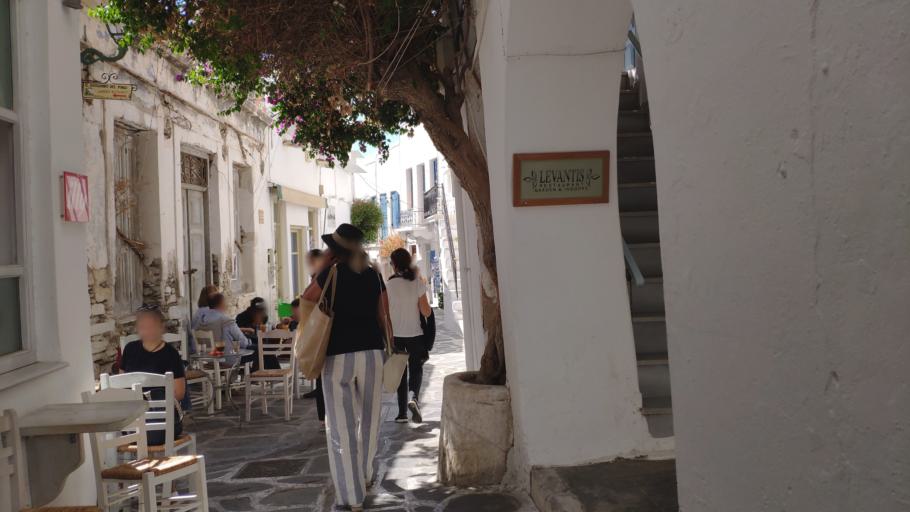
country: GR
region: South Aegean
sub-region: Nomos Kykladon
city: Paros
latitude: 37.0838
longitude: 25.1474
